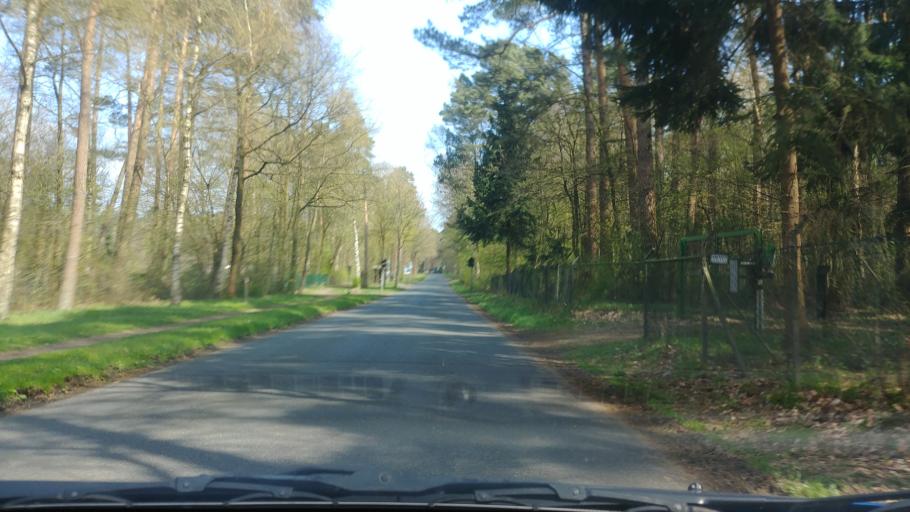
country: DE
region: Lower Saxony
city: Hagenburg
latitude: 52.4947
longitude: 9.3303
